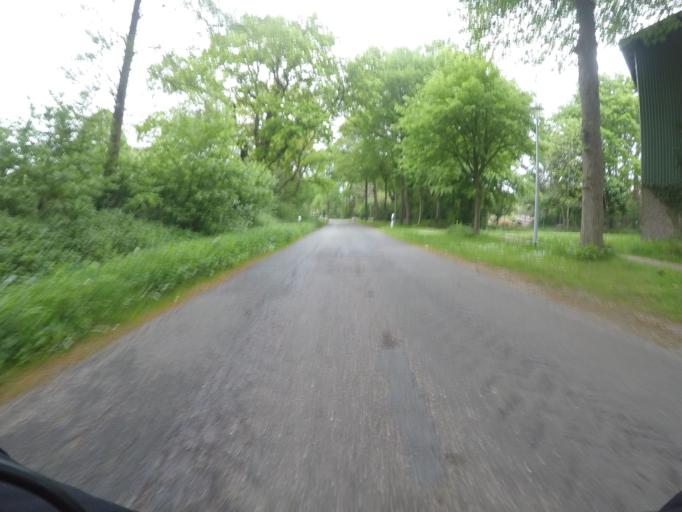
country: DE
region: Schleswig-Holstein
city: Rickling
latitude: 54.0061
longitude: 10.1606
